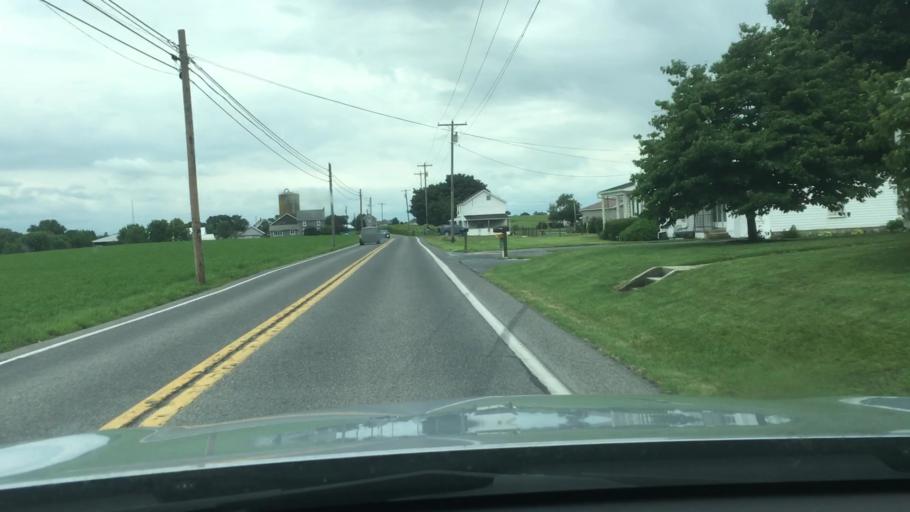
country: US
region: Pennsylvania
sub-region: Franklin County
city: Chambersburg
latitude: 39.8946
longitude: -77.7237
